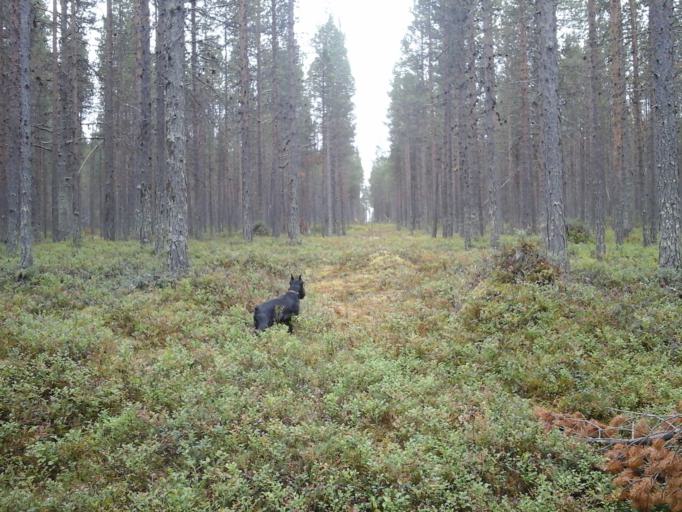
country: RU
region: Murmansk
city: Apatity
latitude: 67.5266
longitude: 33.2435
